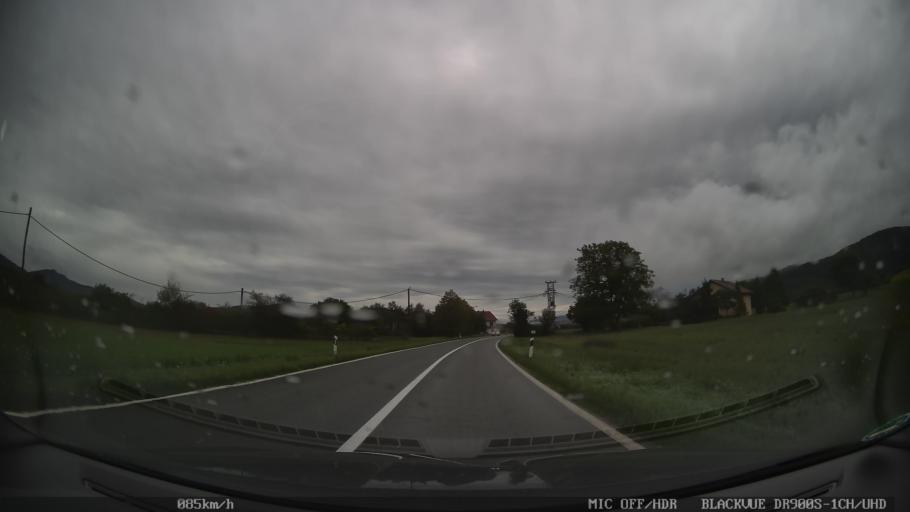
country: HR
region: Licko-Senjska
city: Brinje
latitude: 44.9492
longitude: 15.1249
